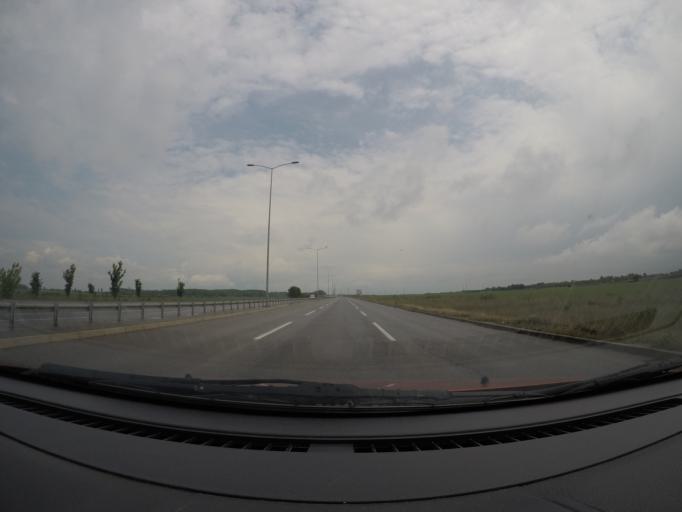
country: RS
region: Central Serbia
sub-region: Belgrade
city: Zemun
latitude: 44.9022
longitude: 20.4392
